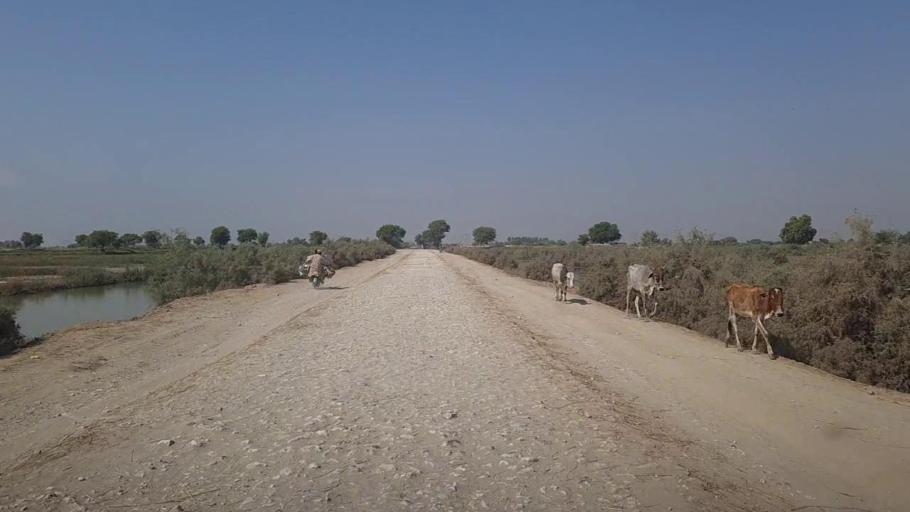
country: PK
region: Sindh
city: Kandhkot
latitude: 28.3886
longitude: 69.3380
